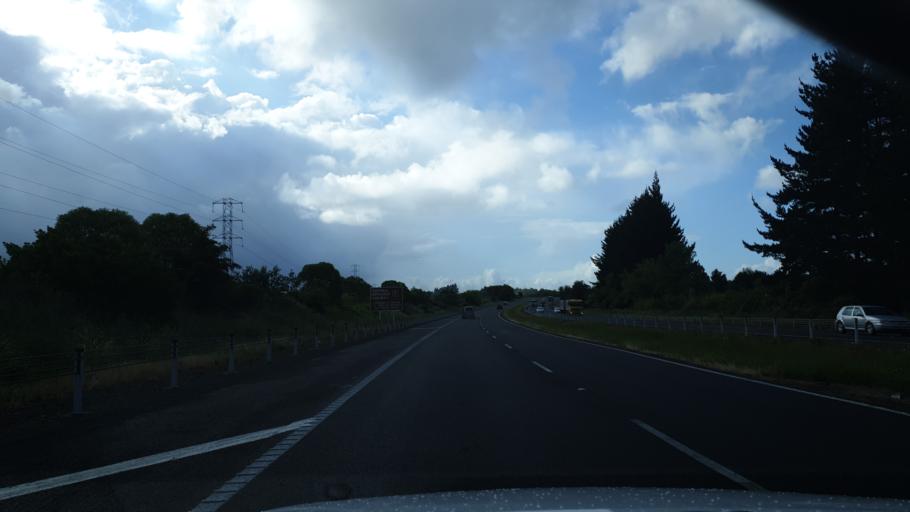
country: NZ
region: Auckland
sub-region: Auckland
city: Pukekohe East
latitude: -37.2425
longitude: 175.0242
